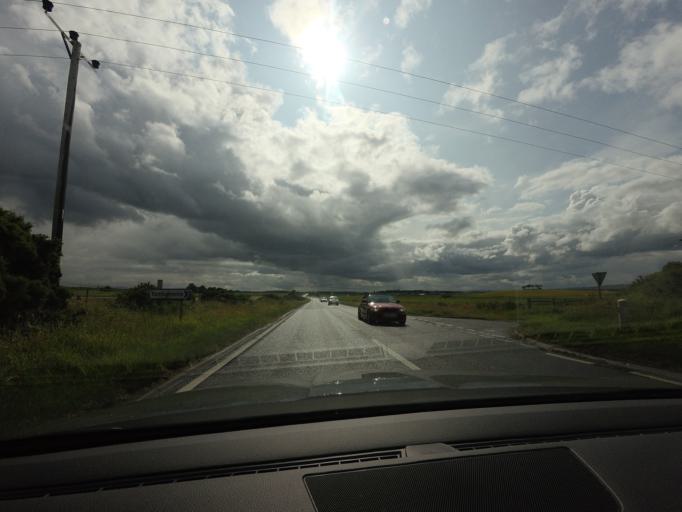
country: GB
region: Scotland
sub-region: Highland
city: Nairn
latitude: 57.5605
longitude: -3.9616
